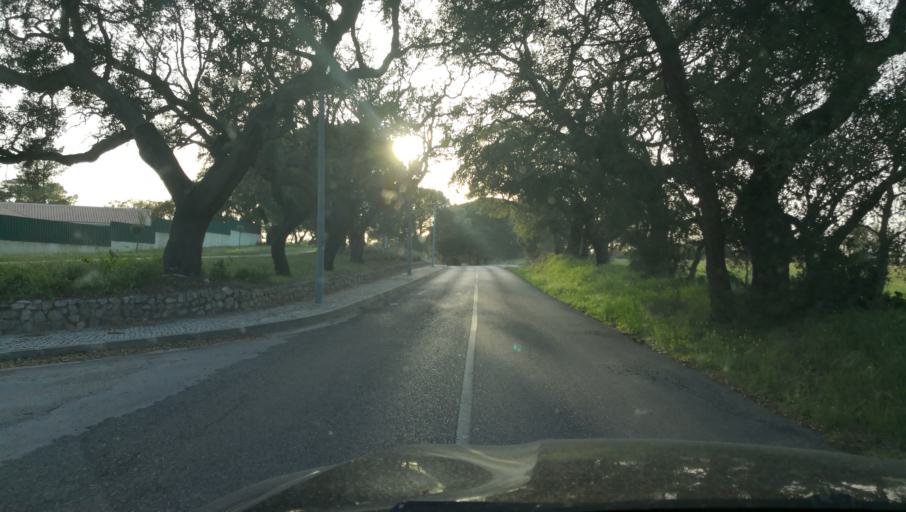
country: PT
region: Setubal
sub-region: Setubal
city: Setubal
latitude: 38.5374
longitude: -8.8261
